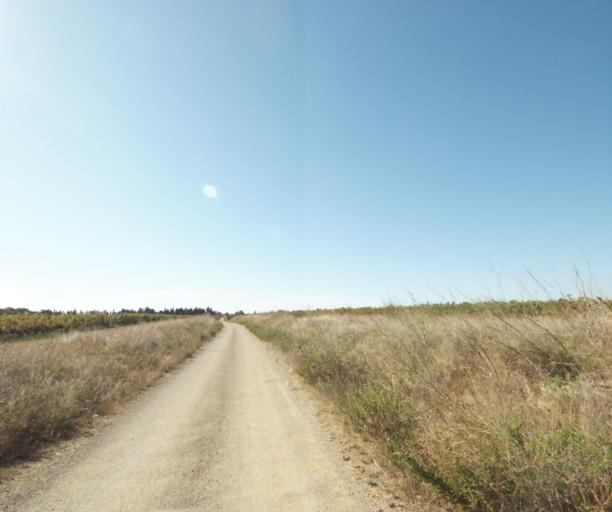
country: FR
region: Languedoc-Roussillon
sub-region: Departement du Gard
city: Bouillargues
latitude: 43.7874
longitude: 4.4104
